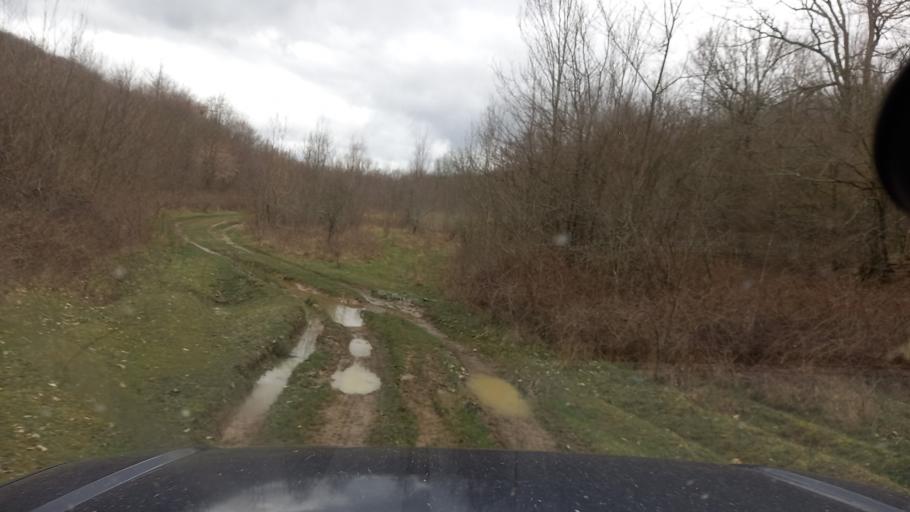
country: RU
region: Krasnodarskiy
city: Pshada
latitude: 44.4875
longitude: 38.3965
